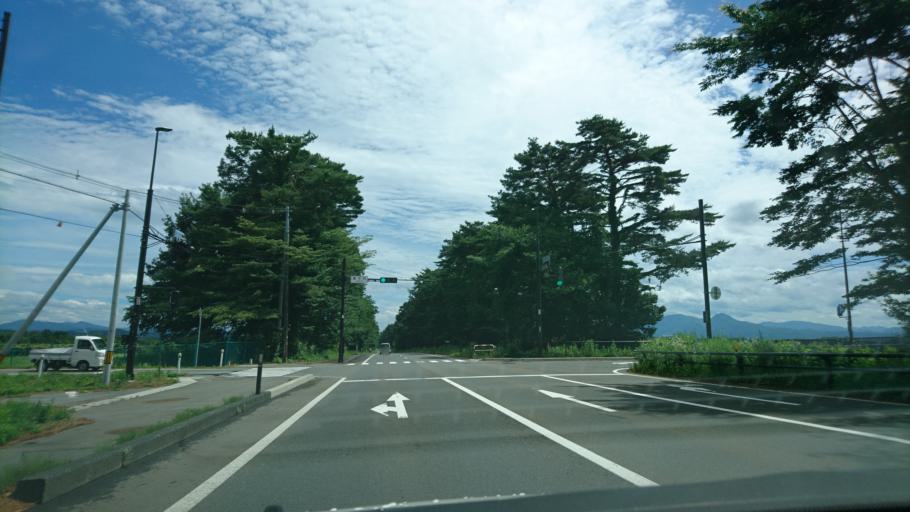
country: JP
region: Iwate
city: Morioka-shi
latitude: 39.7832
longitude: 141.1254
